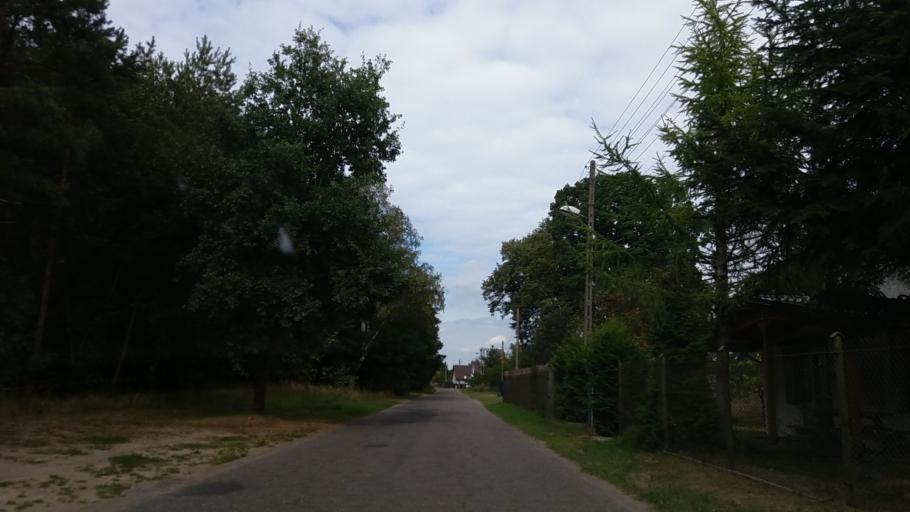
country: PL
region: West Pomeranian Voivodeship
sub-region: Powiat stargardzki
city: Kobylanka
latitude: 53.3396
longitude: 14.8934
